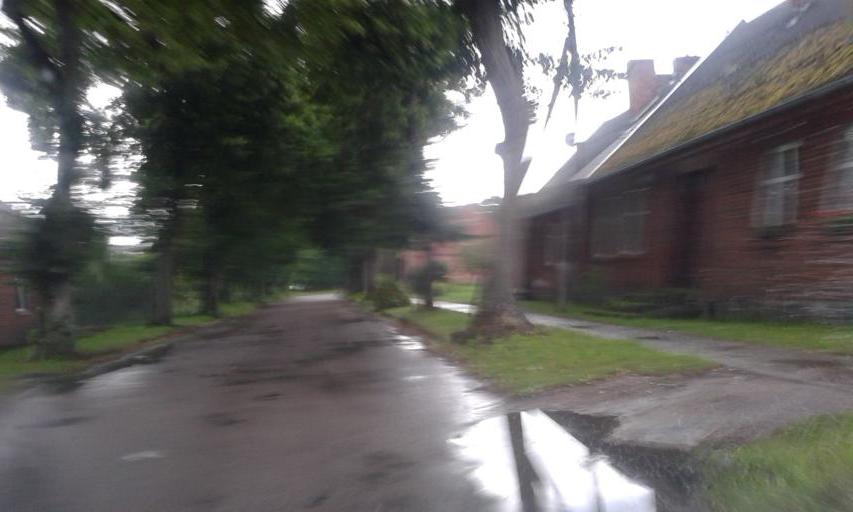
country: PL
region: Greater Poland Voivodeship
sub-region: Powiat zlotowski
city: Sypniewo
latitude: 53.4677
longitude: 16.4973
